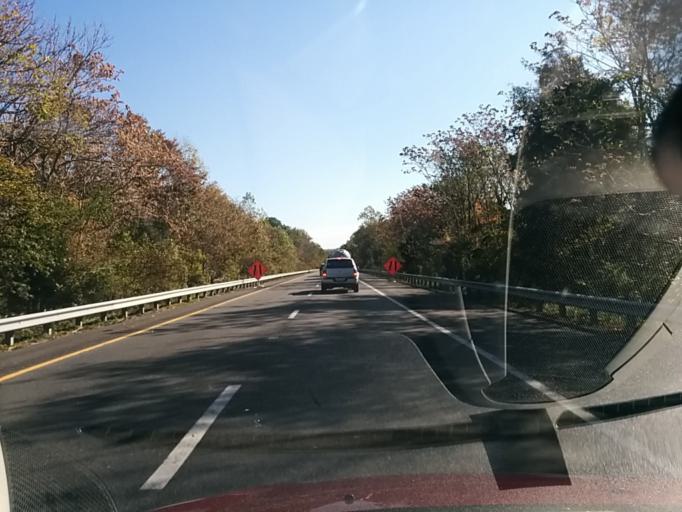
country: US
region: Virginia
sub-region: Albemarle County
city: Crozet
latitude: 38.0347
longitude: -78.6202
